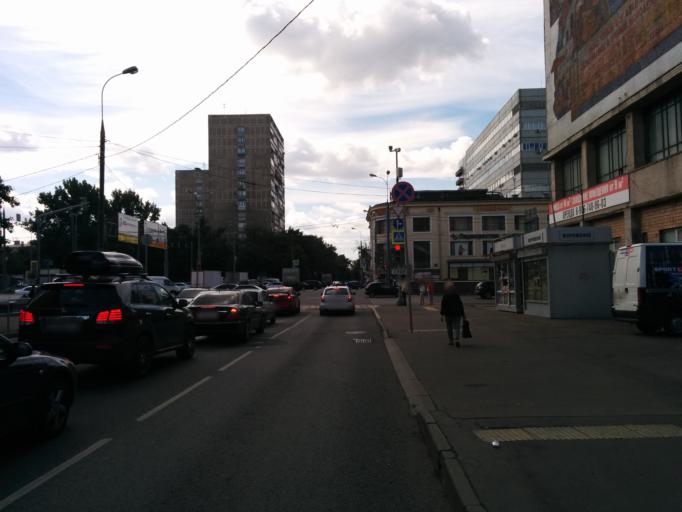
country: RU
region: Moscow
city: Mar'ina Roshcha
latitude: 55.7938
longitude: 37.6130
